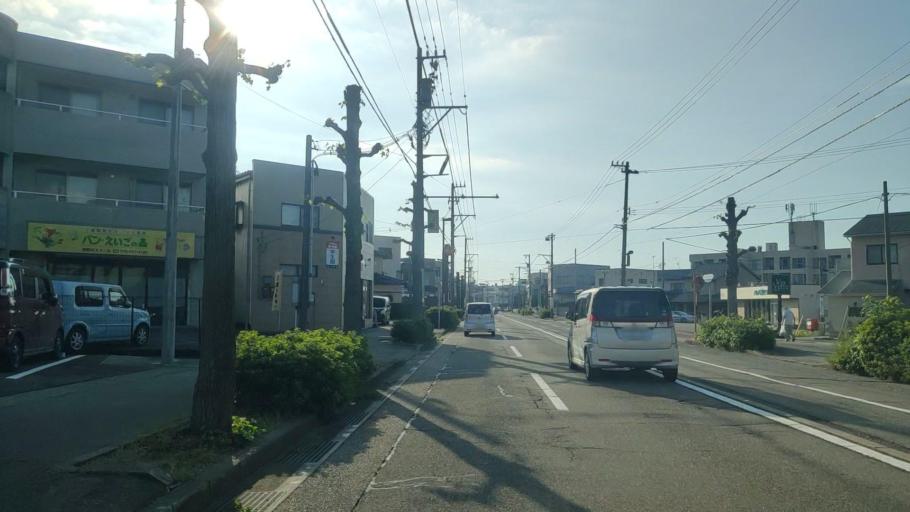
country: JP
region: Ishikawa
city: Kanazawa-shi
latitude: 36.5621
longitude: 136.6746
